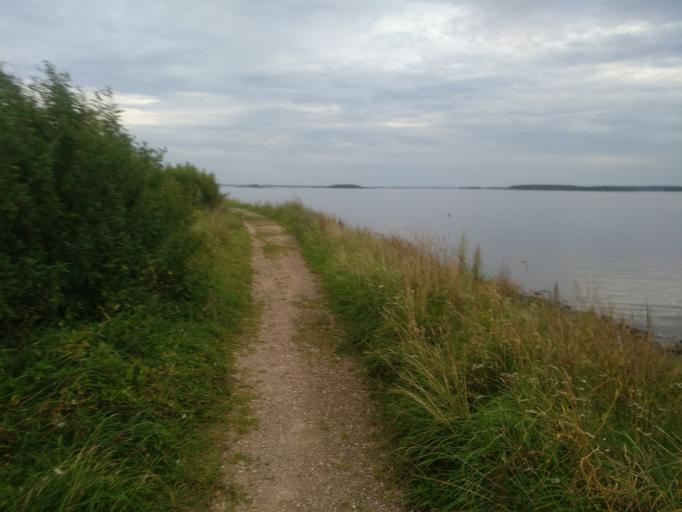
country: RU
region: Tverskaya
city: Vyshniy Volochek
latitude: 57.6061
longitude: 34.4966
